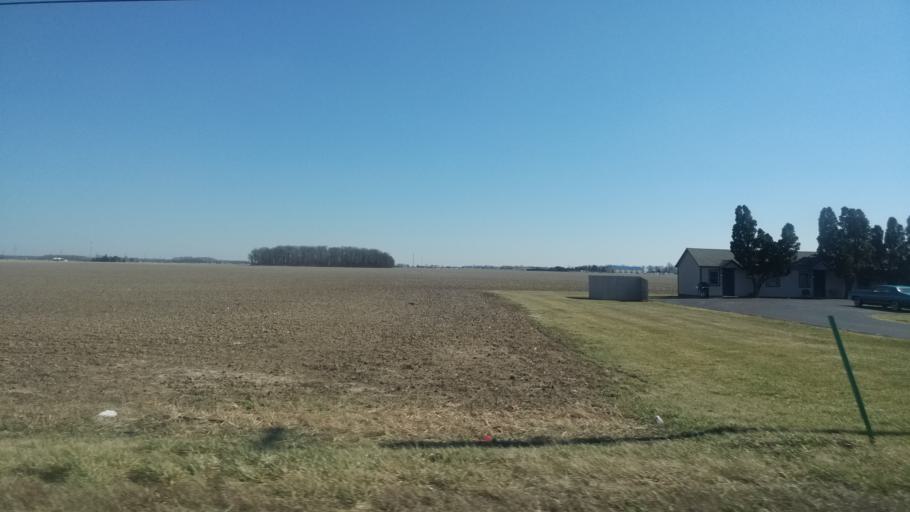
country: US
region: Ohio
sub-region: Wood County
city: Haskins
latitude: 41.4639
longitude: -83.6496
